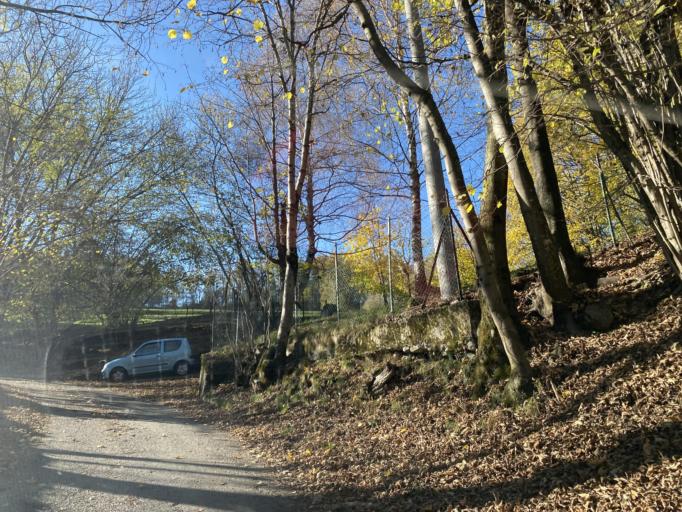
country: IT
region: Lombardy
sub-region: Provincia di Como
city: Pellio Intelvi
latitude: 45.9754
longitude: 9.0577
